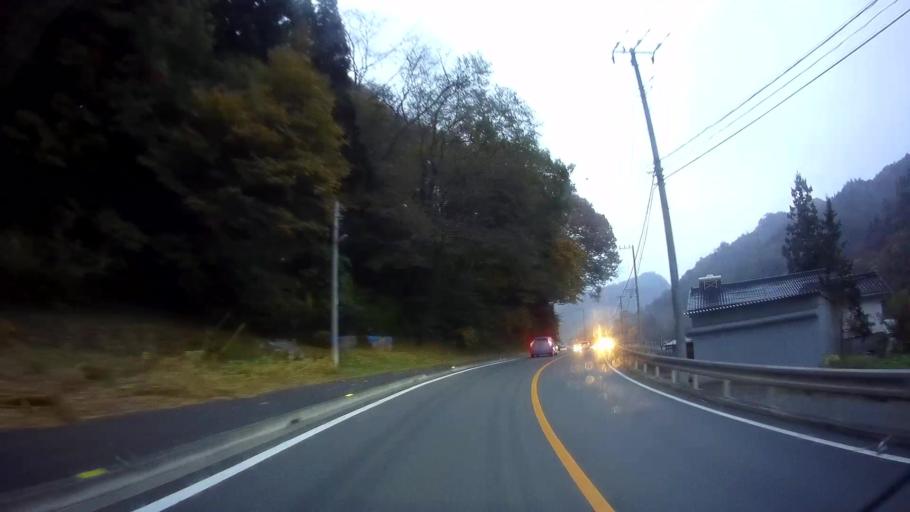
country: JP
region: Gunma
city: Nakanojomachi
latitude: 36.5272
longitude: 138.7812
